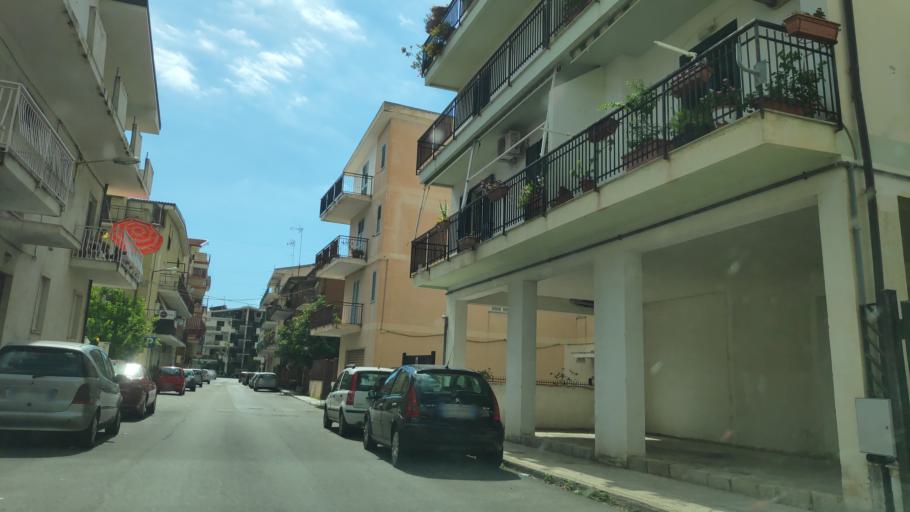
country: IT
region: Calabria
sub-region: Provincia di Cosenza
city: Amantea
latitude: 39.1320
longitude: 16.0727
